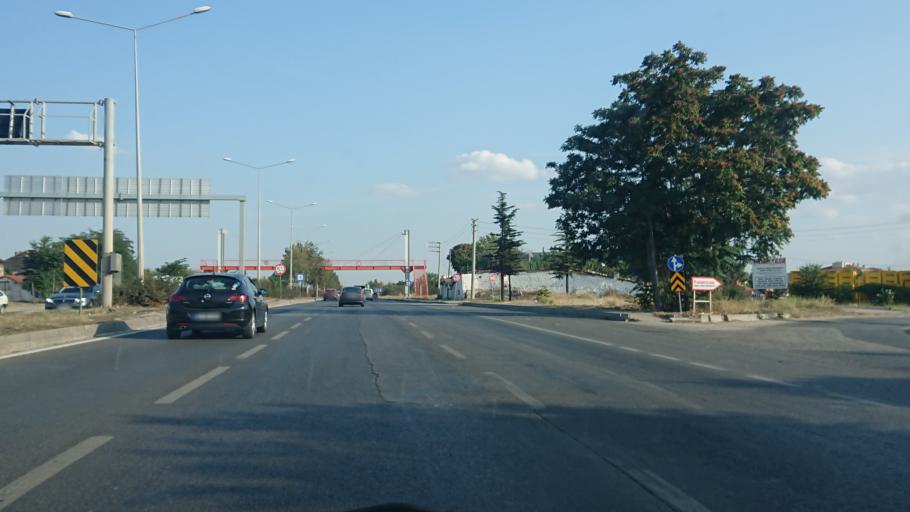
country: TR
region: Eskisehir
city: Eskisehir
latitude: 39.7713
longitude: 30.5597
